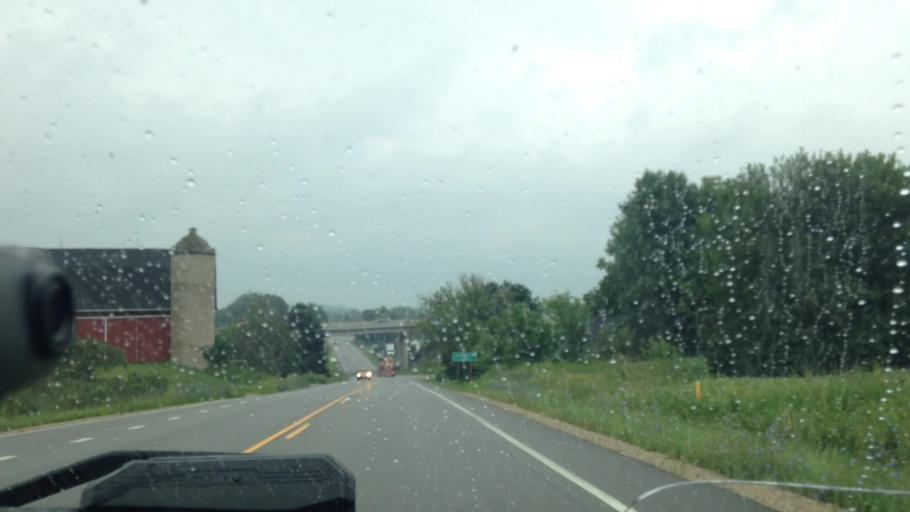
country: US
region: Wisconsin
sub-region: Washington County
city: Slinger
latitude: 43.3133
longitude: -88.2625
